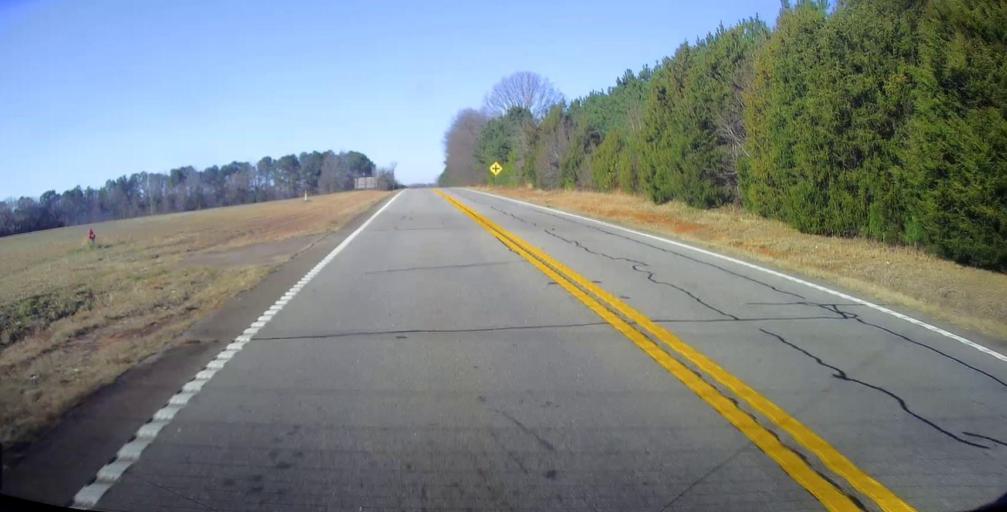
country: US
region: Georgia
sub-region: Meriwether County
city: Manchester
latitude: 32.8988
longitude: -84.5992
